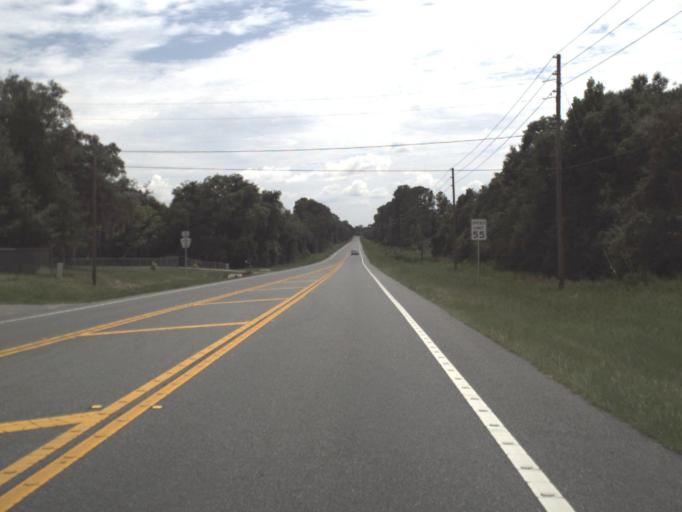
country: US
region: Florida
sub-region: Citrus County
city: Hernando
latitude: 28.9745
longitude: -82.3641
